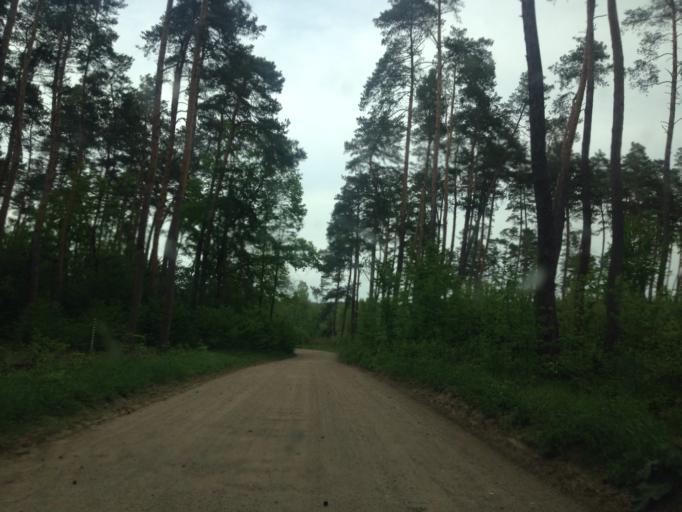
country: PL
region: Kujawsko-Pomorskie
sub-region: Powiat brodnicki
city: Bartniczka
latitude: 53.2777
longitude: 19.5799
